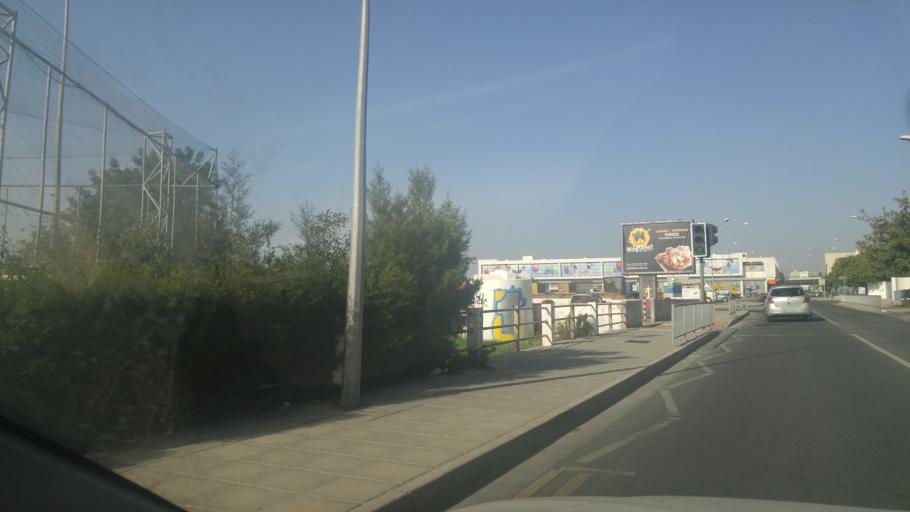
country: CY
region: Limassol
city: Limassol
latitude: 34.6866
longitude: 33.0136
